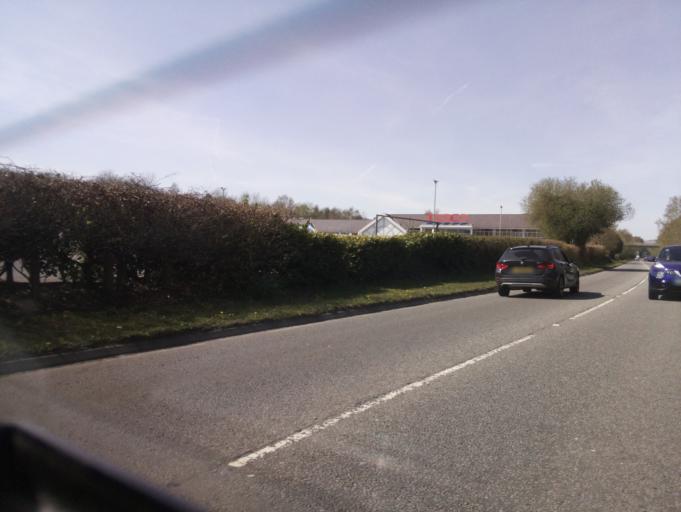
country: GB
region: Wales
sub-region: Rhondda Cynon Taf
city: Aberdare
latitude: 51.7173
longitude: -3.4465
